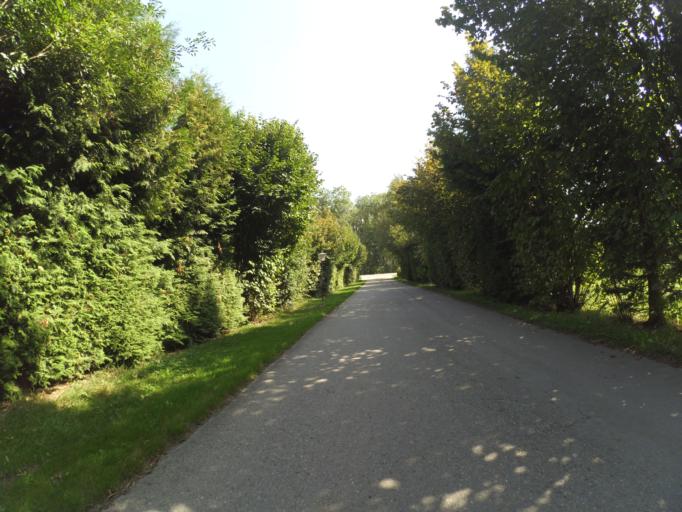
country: DE
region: Bavaria
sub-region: Upper Bavaria
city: Hurlach
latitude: 48.1094
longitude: 10.7754
